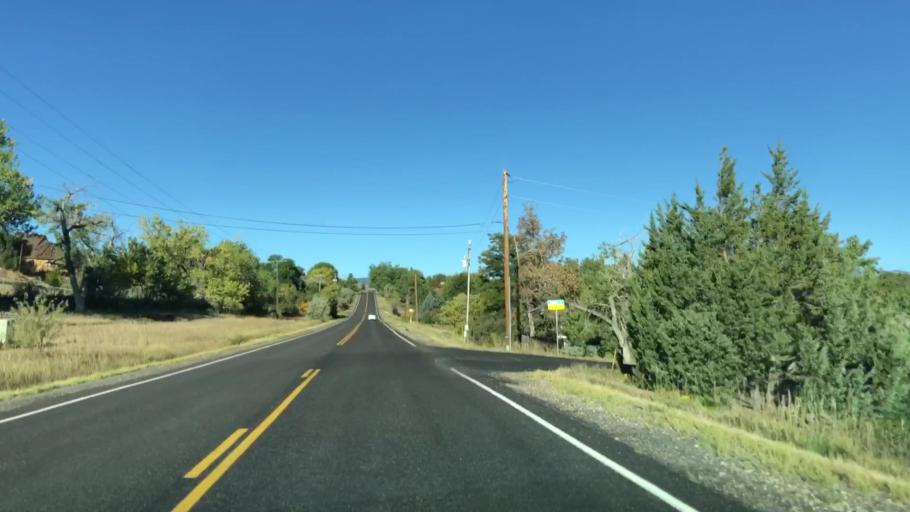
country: US
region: Colorado
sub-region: Larimer County
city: Loveland
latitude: 40.3786
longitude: -105.1474
